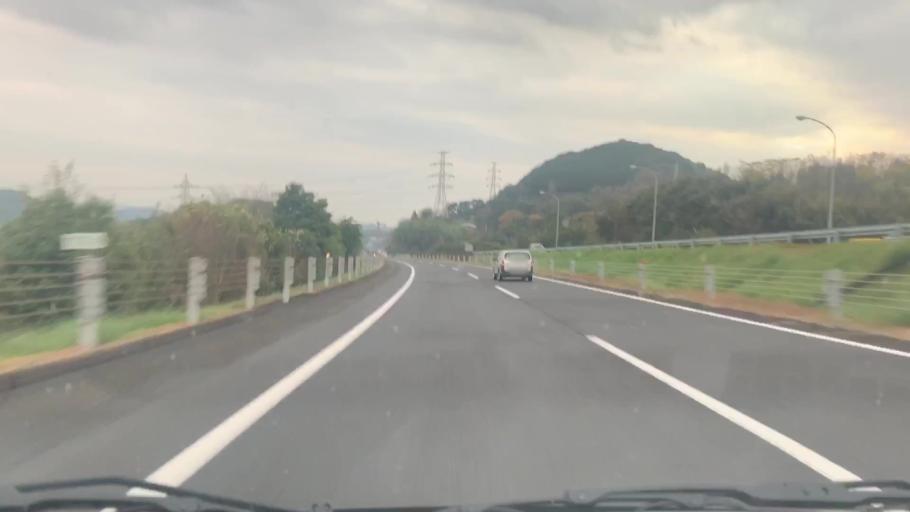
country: JP
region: Nagasaki
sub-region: Isahaya-shi
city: Isahaya
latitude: 32.8605
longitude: 130.0027
